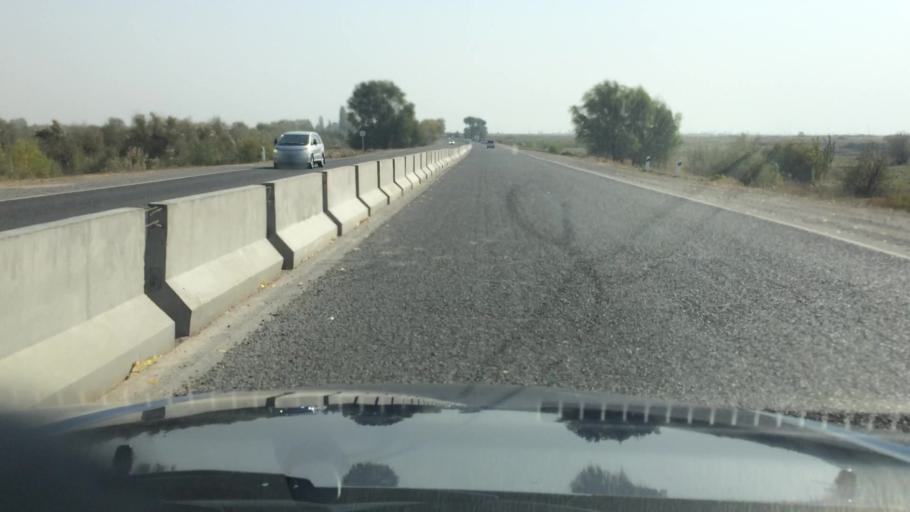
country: KG
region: Chuy
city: Kant
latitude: 42.9610
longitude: 74.9207
